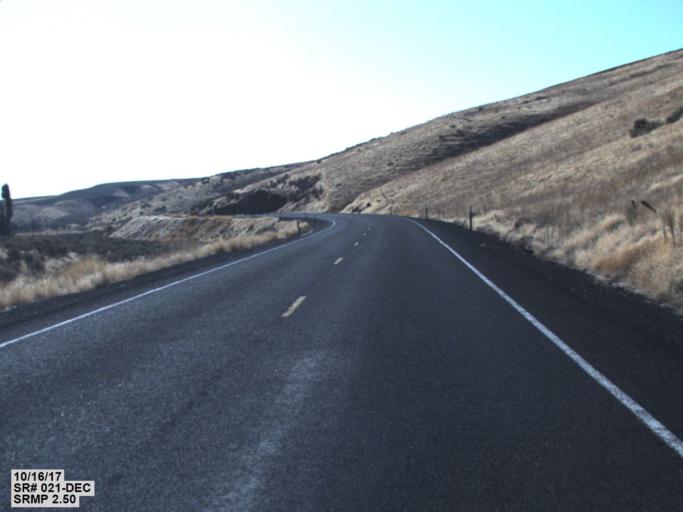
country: US
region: Washington
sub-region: Franklin County
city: Connell
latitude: 46.6763
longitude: -118.5424
